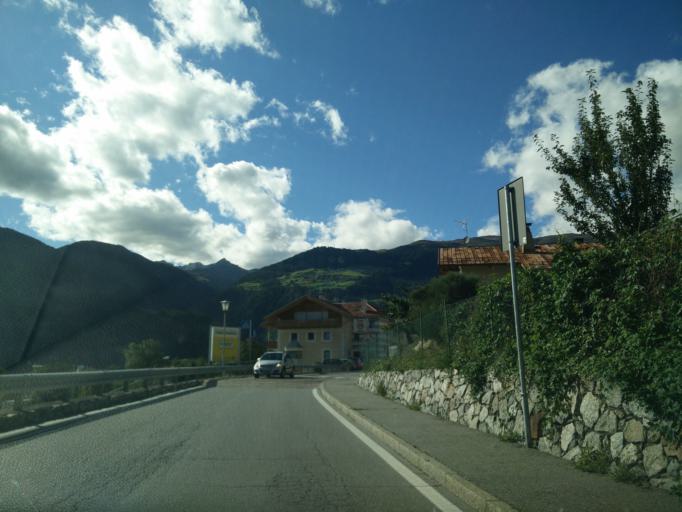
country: IT
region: Trentino-Alto Adige
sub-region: Bolzano
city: Malles Venosta
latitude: 46.6866
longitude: 10.5510
